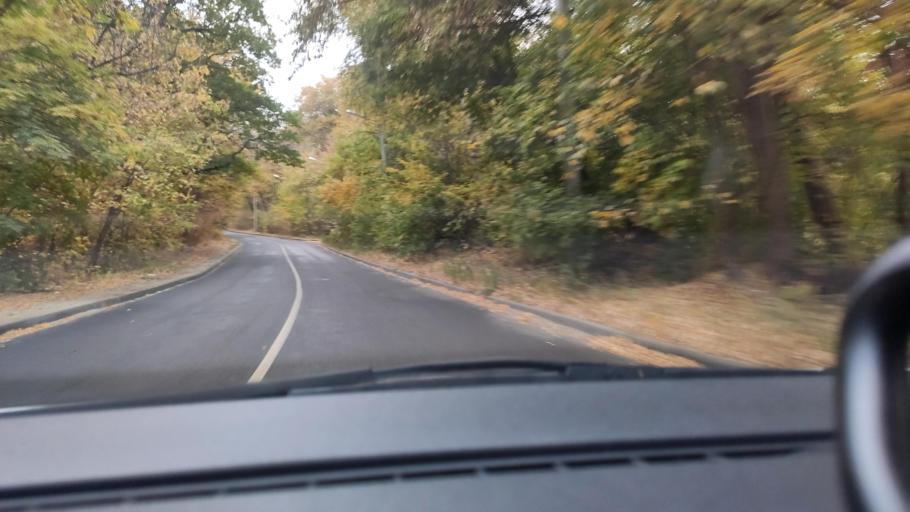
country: RU
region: Voronezj
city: Voronezh
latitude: 51.7208
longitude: 39.2351
